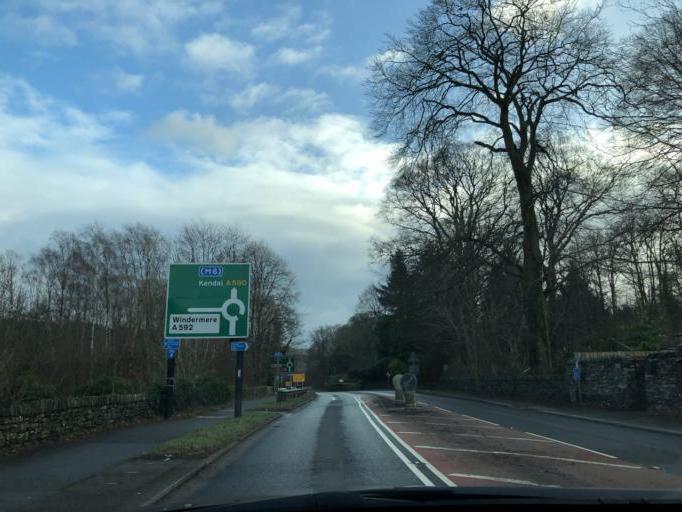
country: GB
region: England
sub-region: Cumbria
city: Grange-over-Sands
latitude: 54.2681
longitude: -2.9700
